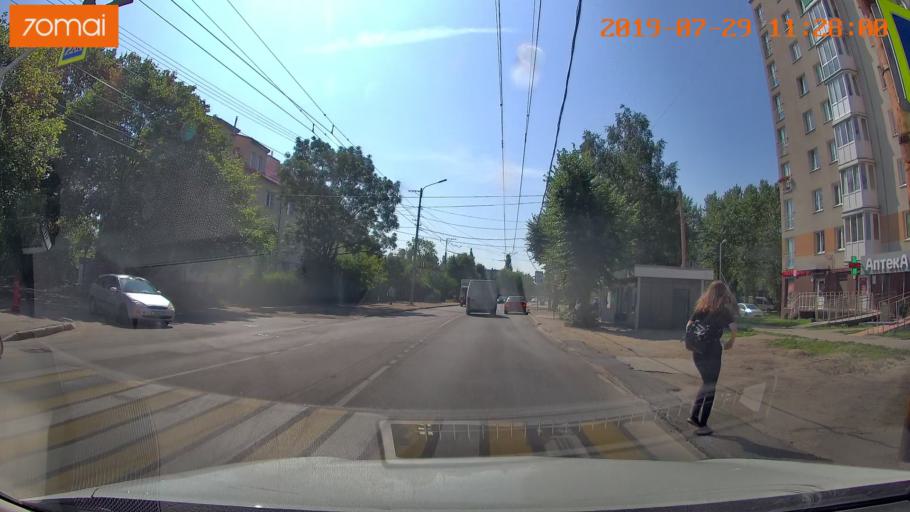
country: RU
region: Kaliningrad
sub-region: Gorod Kaliningrad
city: Kaliningrad
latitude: 54.6891
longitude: 20.5318
